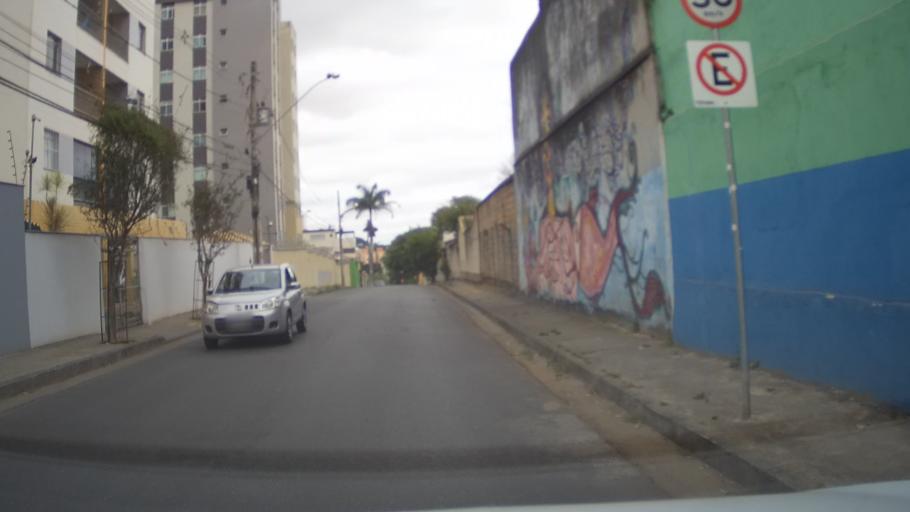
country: BR
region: Minas Gerais
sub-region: Belo Horizonte
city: Belo Horizonte
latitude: -19.8564
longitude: -43.9497
